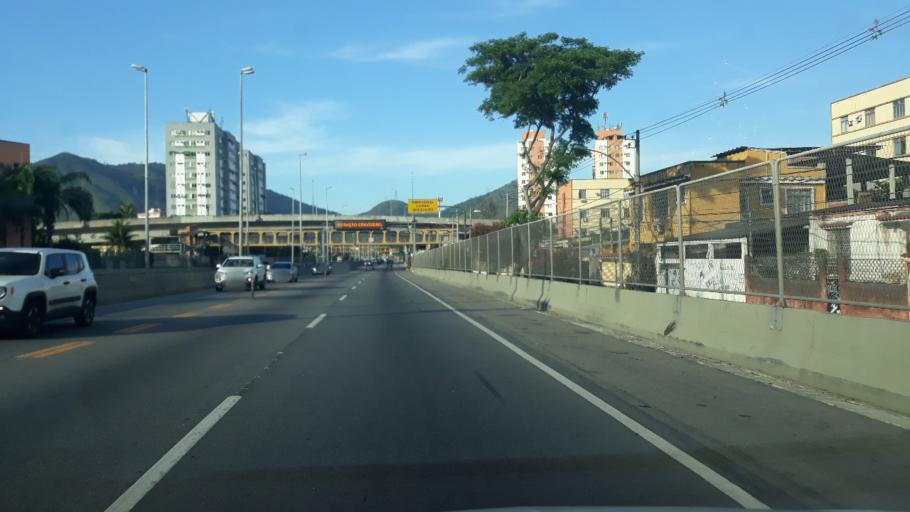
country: BR
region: Rio de Janeiro
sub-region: Rio De Janeiro
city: Rio de Janeiro
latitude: -22.8882
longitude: -43.2942
